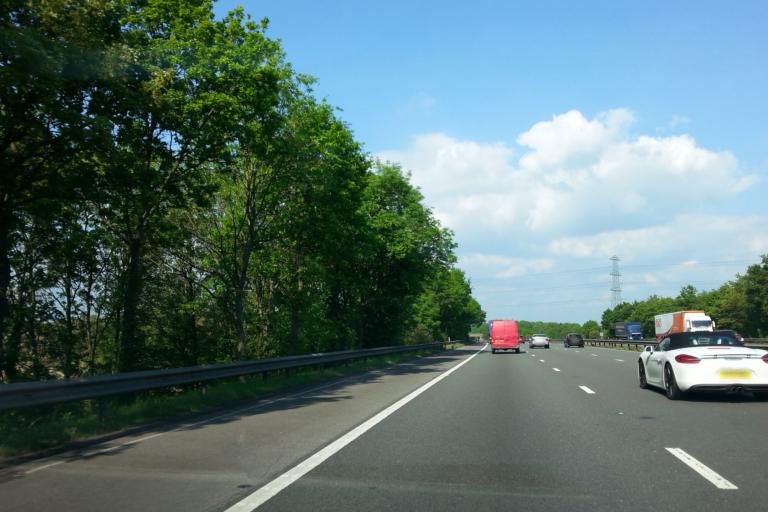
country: GB
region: England
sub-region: Leicestershire
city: Stoney Stanton
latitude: 52.5658
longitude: -1.2809
